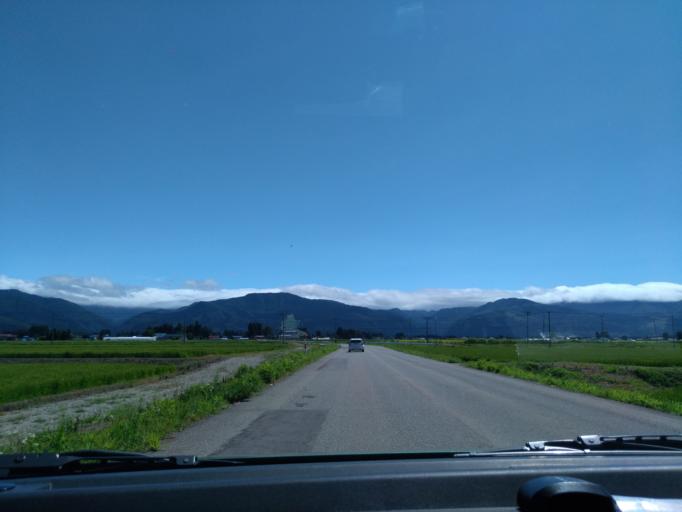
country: JP
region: Akita
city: Kakunodatemachi
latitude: 39.5309
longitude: 140.5933
